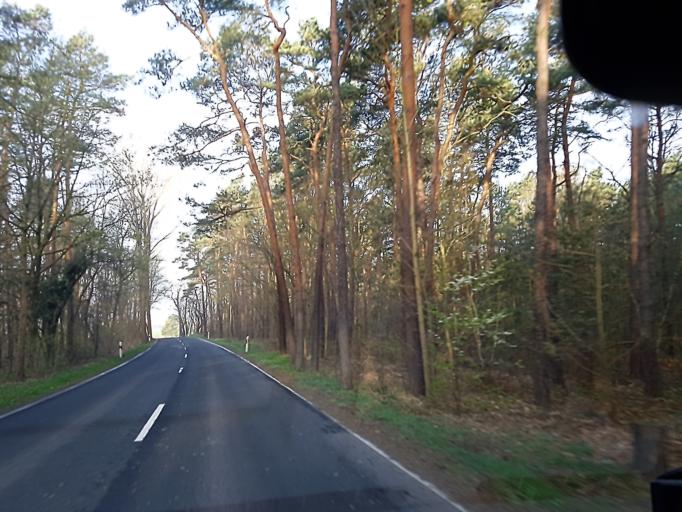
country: DE
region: Saxony
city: Strehla
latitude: 51.3792
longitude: 13.2720
